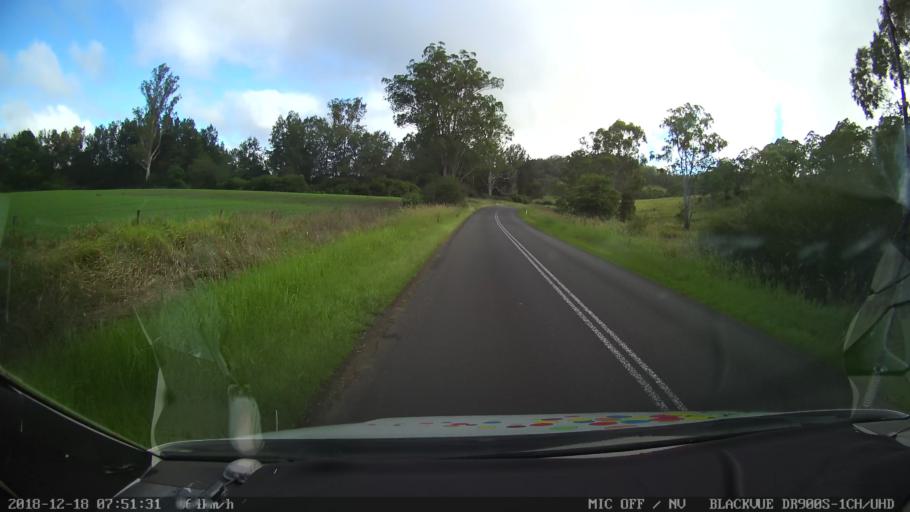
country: AU
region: New South Wales
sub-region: Kyogle
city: Kyogle
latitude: -28.4368
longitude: 152.5790
